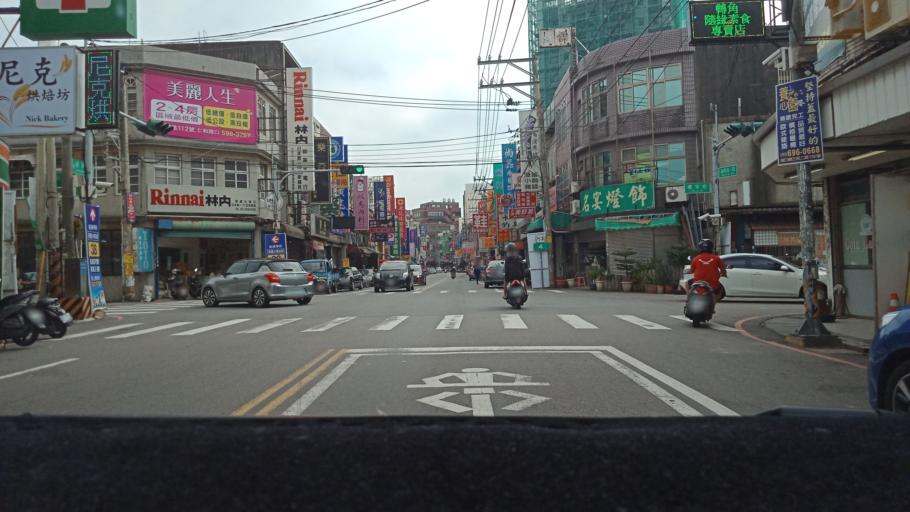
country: TW
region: Taiwan
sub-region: Hsinchu
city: Zhubei
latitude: 24.8734
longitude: 120.9949
